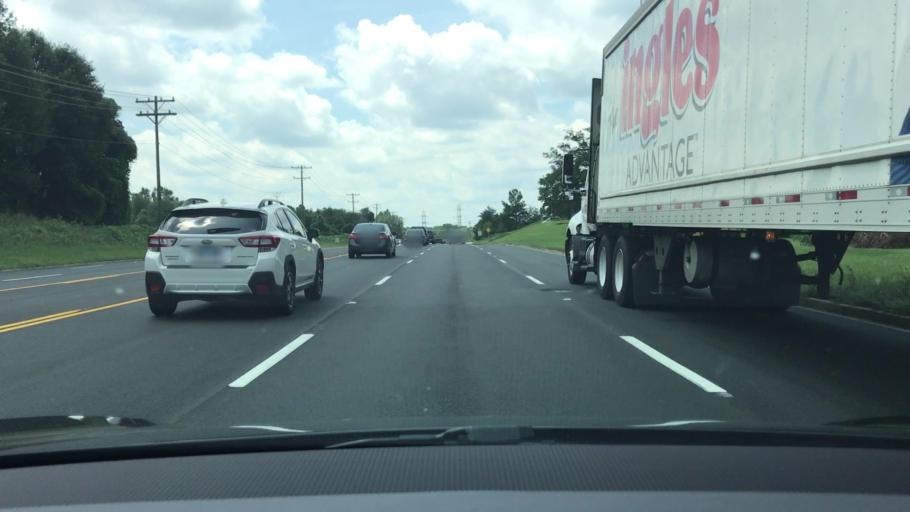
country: US
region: South Carolina
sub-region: Greenville County
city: Berea
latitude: 34.9200
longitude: -82.4596
